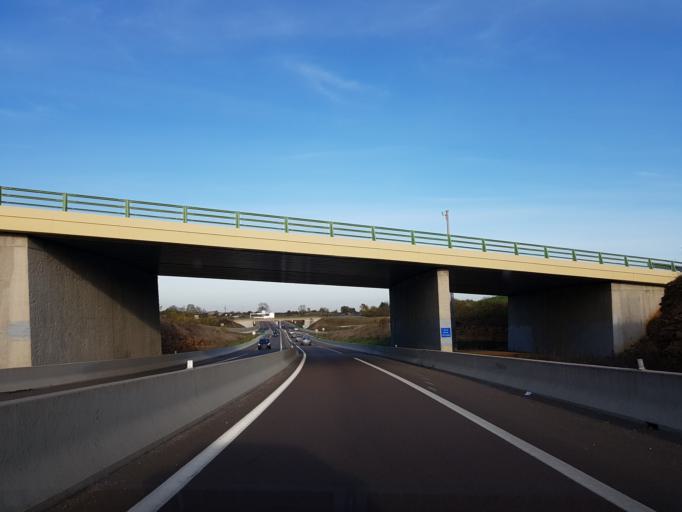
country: FR
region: Bourgogne
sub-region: Departement de la Cote-d'Or
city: Daix
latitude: 47.3469
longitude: 5.0064
